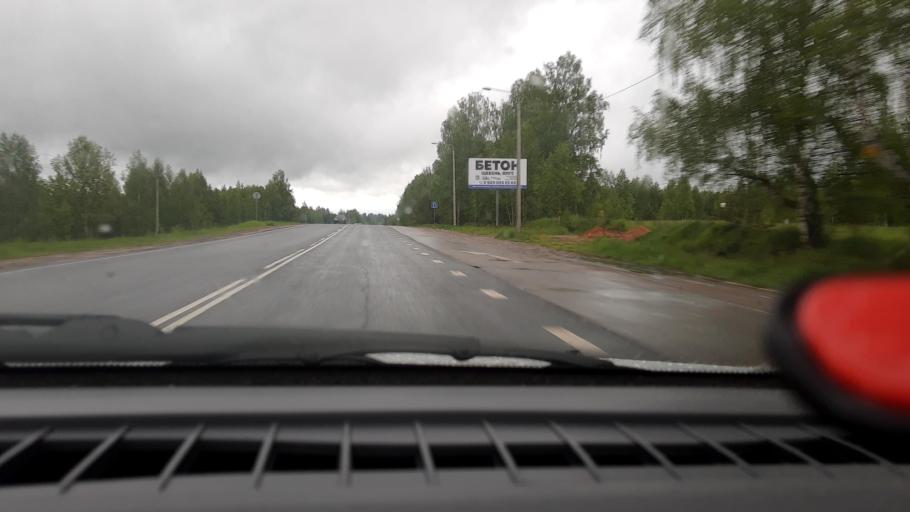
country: RU
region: Nizjnij Novgorod
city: Semenov
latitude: 56.8230
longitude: 44.5839
